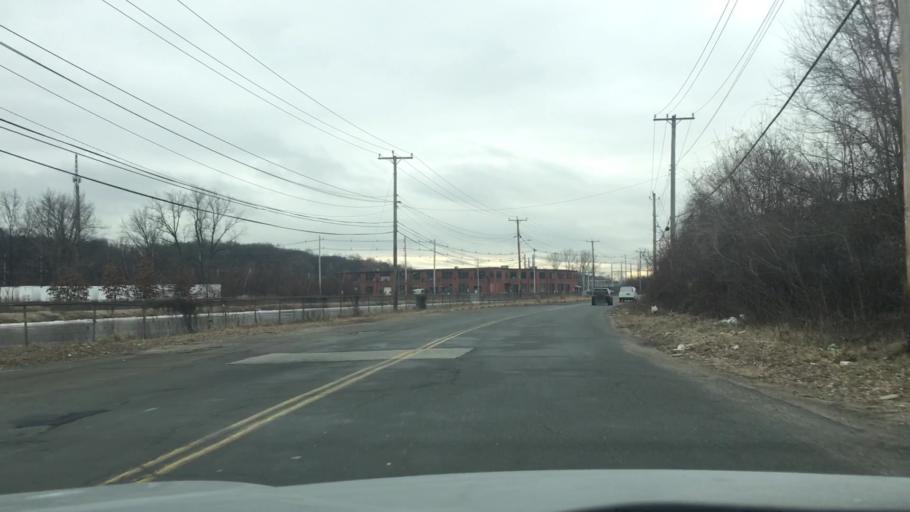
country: US
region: Massachusetts
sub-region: Hampden County
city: North Chicopee
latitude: 42.2038
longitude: -72.5948
